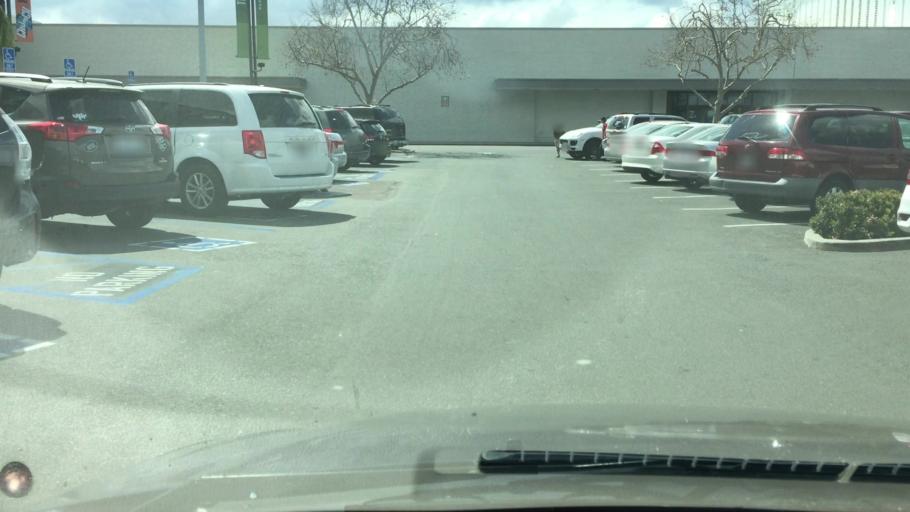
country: US
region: California
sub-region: San Diego County
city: El Cajon
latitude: 32.8069
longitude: -116.9689
